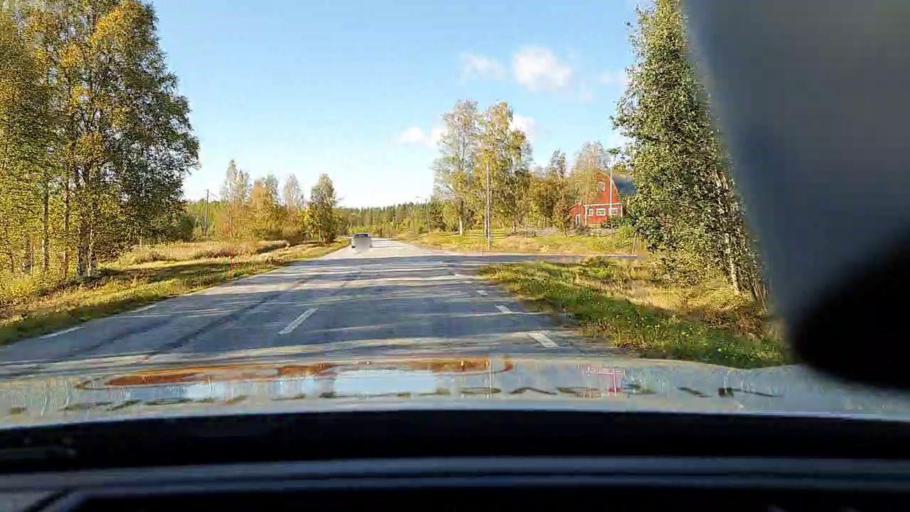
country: SE
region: Norrbotten
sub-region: Pitea Kommun
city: Norrfjarden
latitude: 65.4311
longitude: 21.4895
